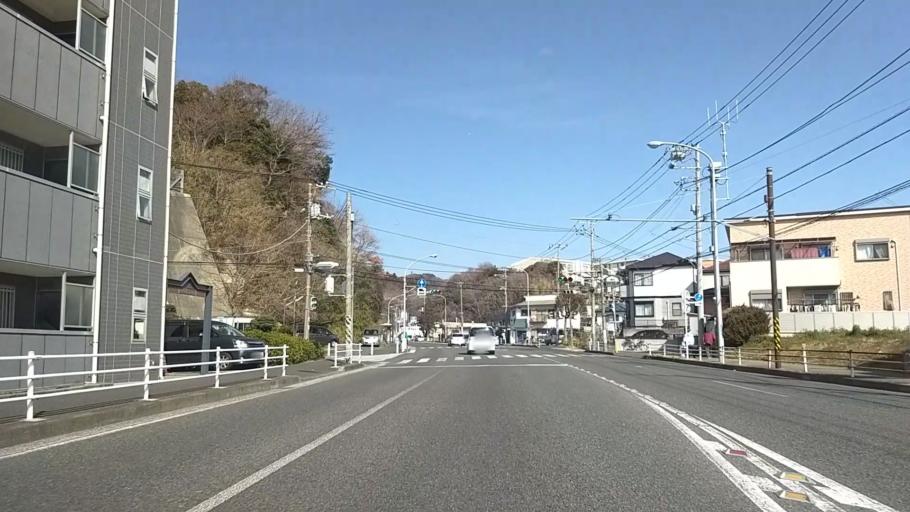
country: JP
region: Kanagawa
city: Zushi
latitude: 35.3480
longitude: 139.6082
